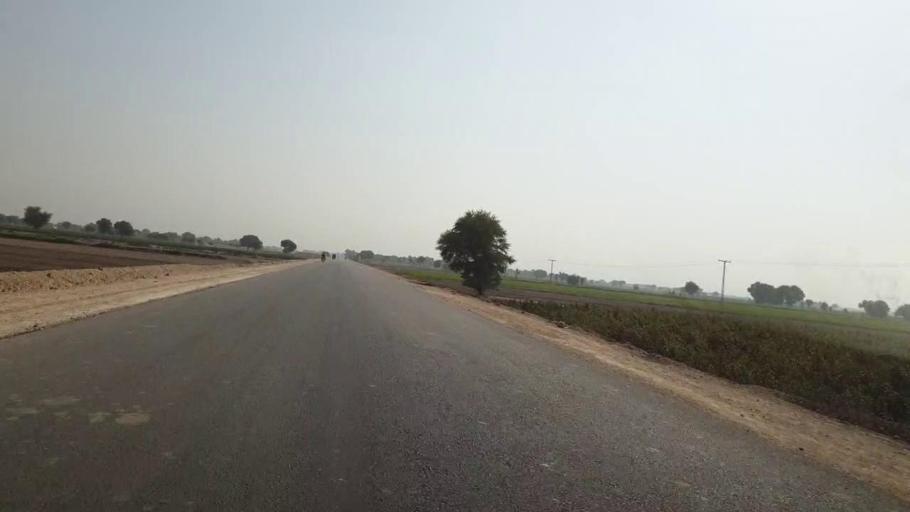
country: PK
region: Sindh
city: Dadu
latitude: 26.6579
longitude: 67.7764
